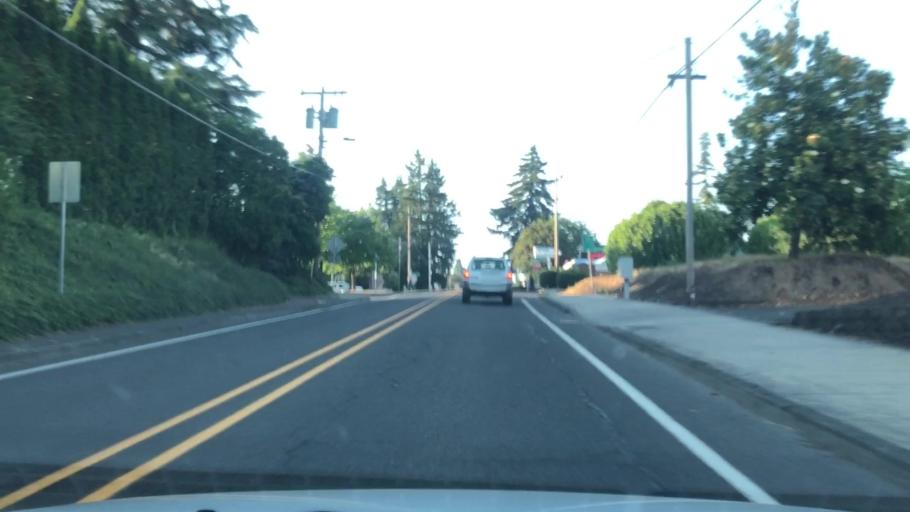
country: US
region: Oregon
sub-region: Clackamas County
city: Oak Grove
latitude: 45.4159
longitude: -122.6455
